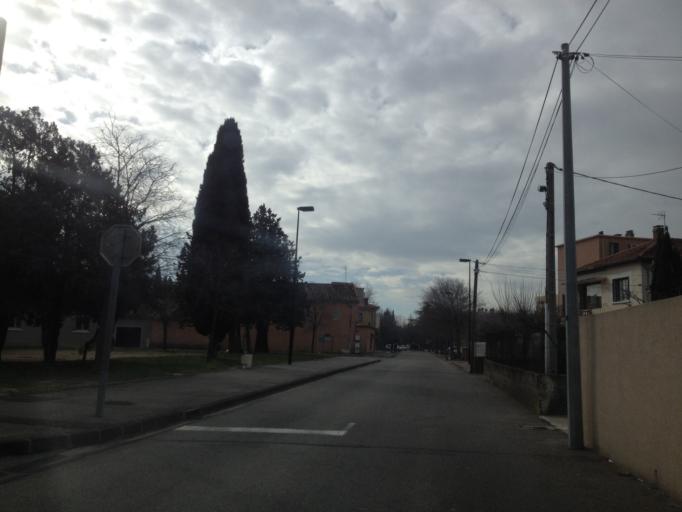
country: FR
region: Provence-Alpes-Cote d'Azur
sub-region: Departement du Vaucluse
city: Orange
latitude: 44.1492
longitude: 4.8051
